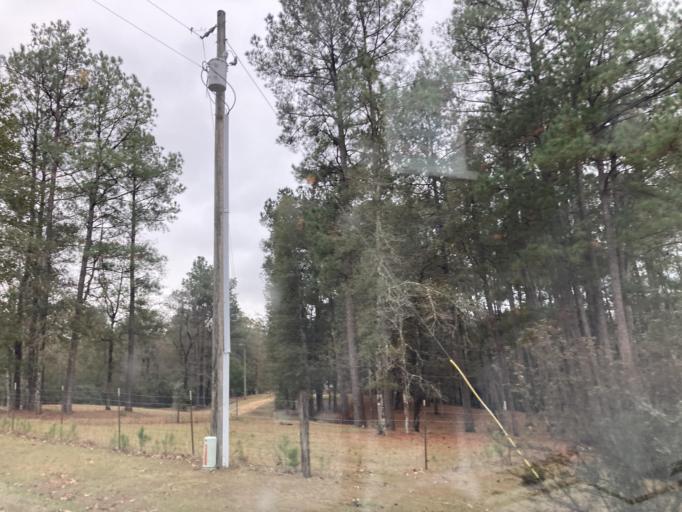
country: US
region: Mississippi
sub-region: Lamar County
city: Purvis
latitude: 31.1984
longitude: -89.4297
